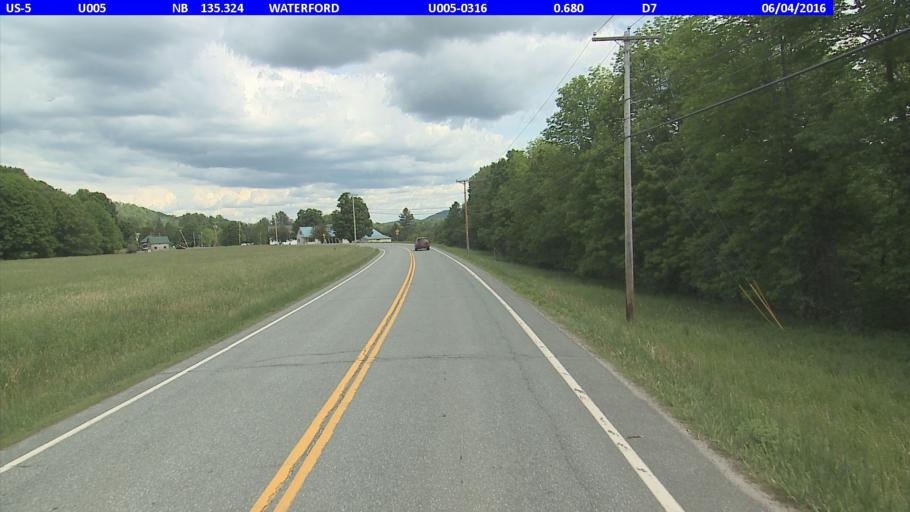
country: US
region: Vermont
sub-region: Caledonia County
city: Saint Johnsbury
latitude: 44.3888
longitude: -72.0240
